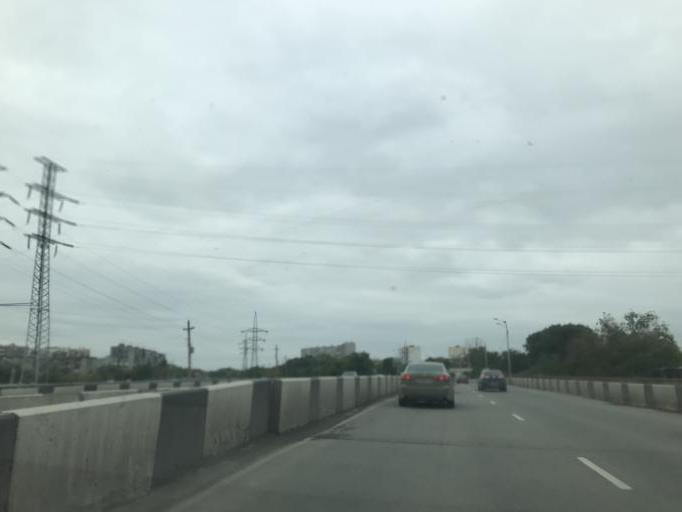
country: RU
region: Chelyabinsk
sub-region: Gorod Chelyabinsk
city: Chelyabinsk
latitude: 55.1676
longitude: 61.4286
